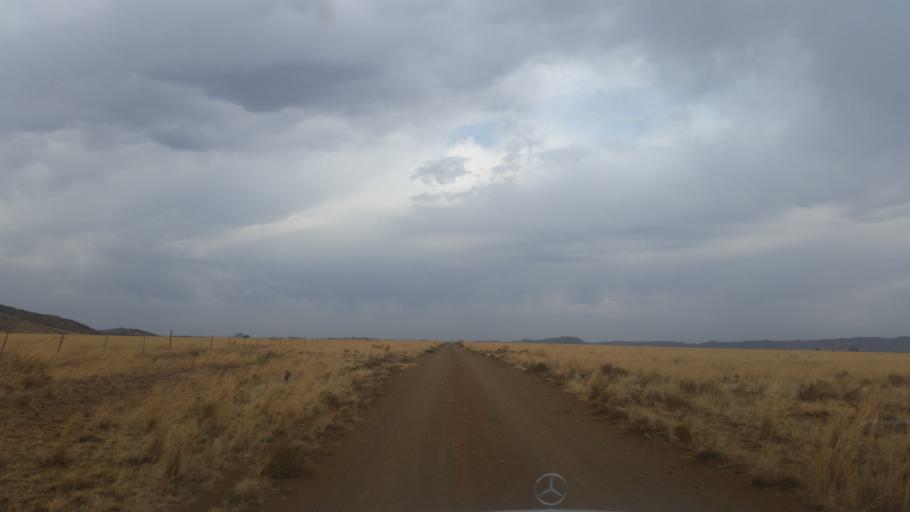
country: ZA
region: Orange Free State
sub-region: Xhariep District Municipality
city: Trompsburg
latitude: -30.5070
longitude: 25.9217
